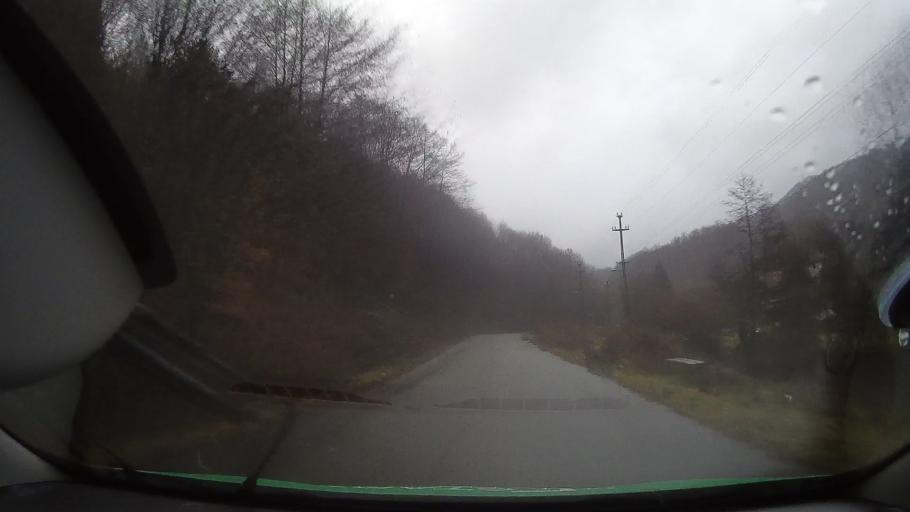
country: RO
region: Alba
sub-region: Comuna Avram Iancu
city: Avram Iancu
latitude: 46.2972
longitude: 22.7571
